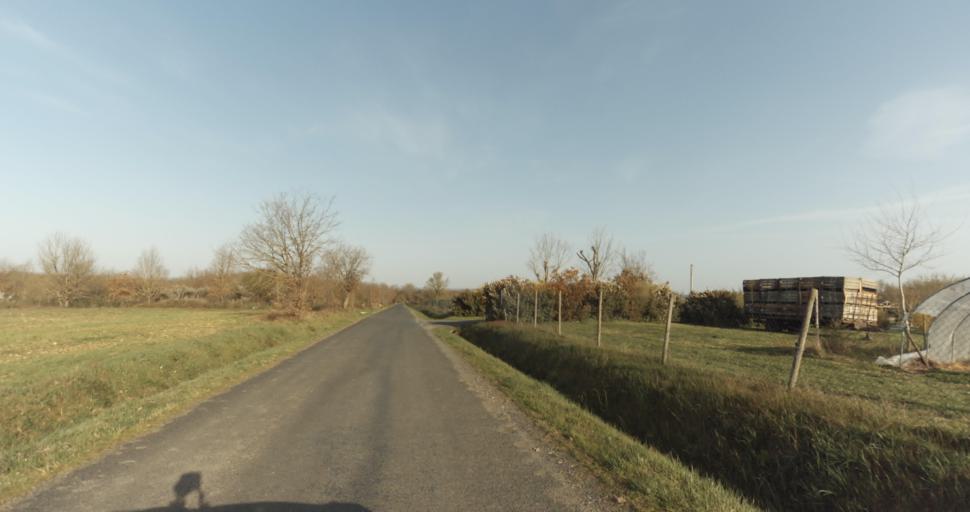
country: FR
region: Midi-Pyrenees
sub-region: Departement du Tarn
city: Saint-Sulpice-la-Pointe
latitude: 43.7346
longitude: 1.6931
